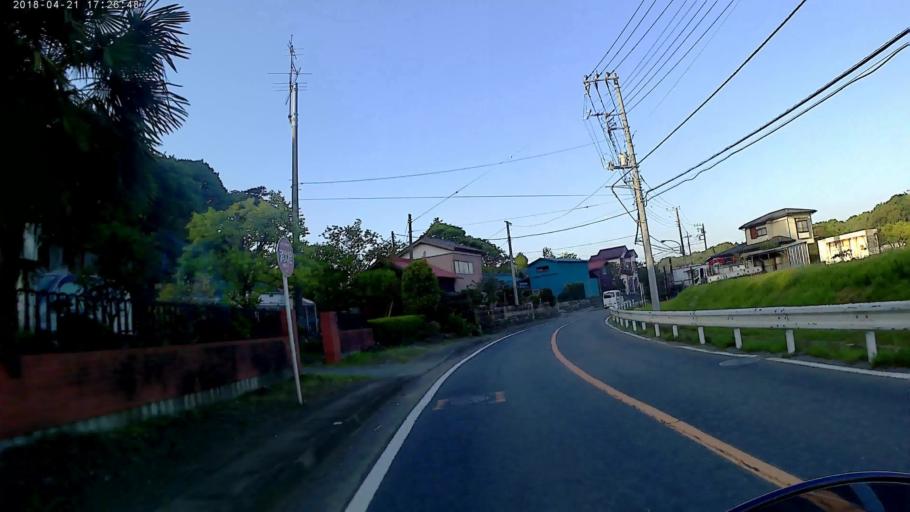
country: JP
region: Kanagawa
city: Atsugi
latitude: 35.4136
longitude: 139.4095
